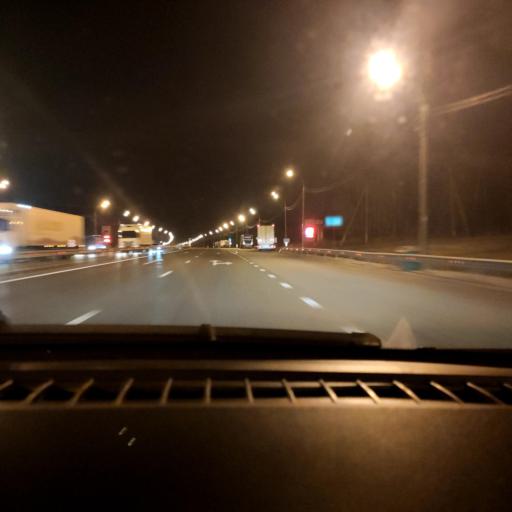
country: RU
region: Lipetsk
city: Khlevnoye
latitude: 52.1280
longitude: 39.1967
